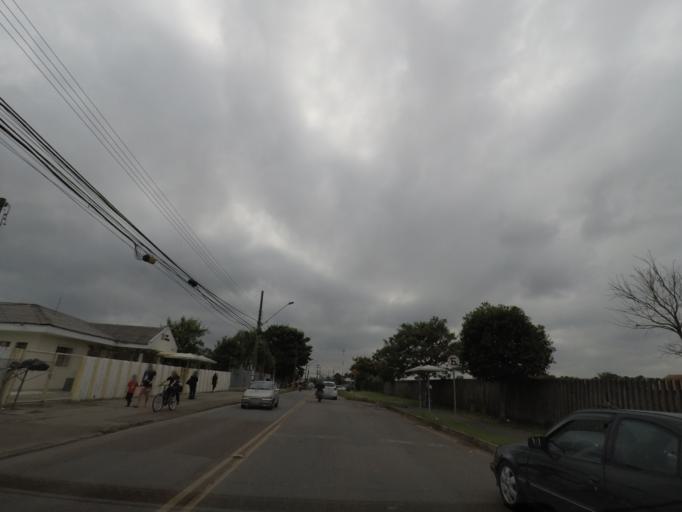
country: BR
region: Parana
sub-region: Curitiba
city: Curitiba
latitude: -25.4959
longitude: -49.3352
